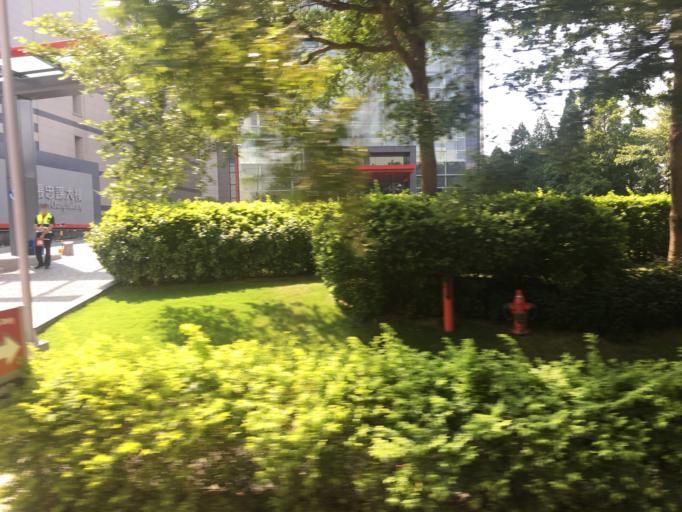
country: TW
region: Taiwan
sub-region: Hsinchu
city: Hsinchu
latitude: 24.7728
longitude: 121.0144
